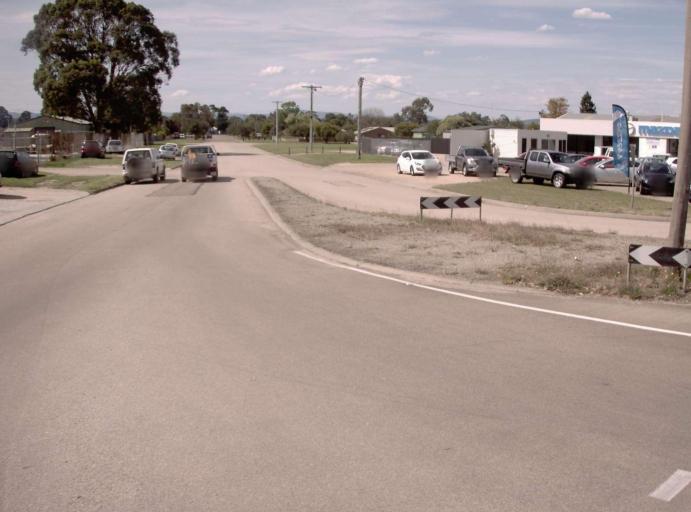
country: AU
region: Victoria
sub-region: East Gippsland
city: Bairnsdale
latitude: -37.8349
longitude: 147.6027
